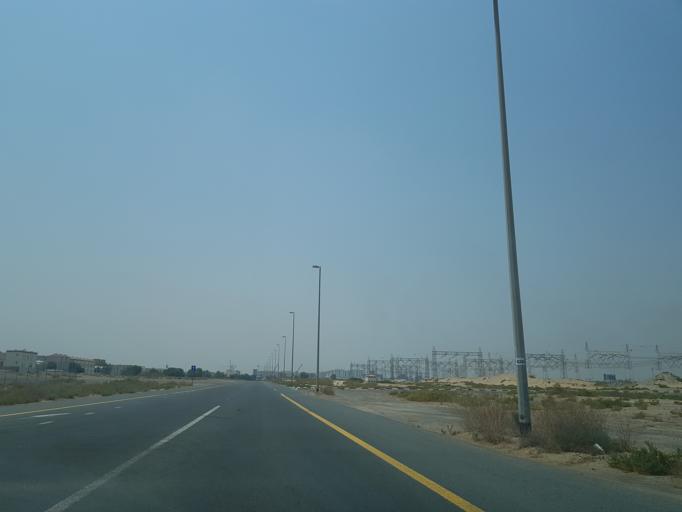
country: AE
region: Ash Shariqah
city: Sharjah
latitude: 25.2331
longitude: 55.4101
